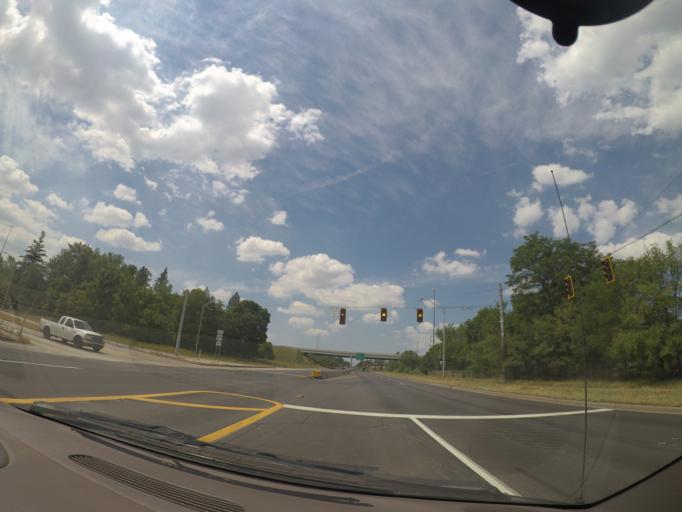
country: US
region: Indiana
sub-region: Elkhart County
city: Dunlap
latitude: 41.6504
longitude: -85.9396
